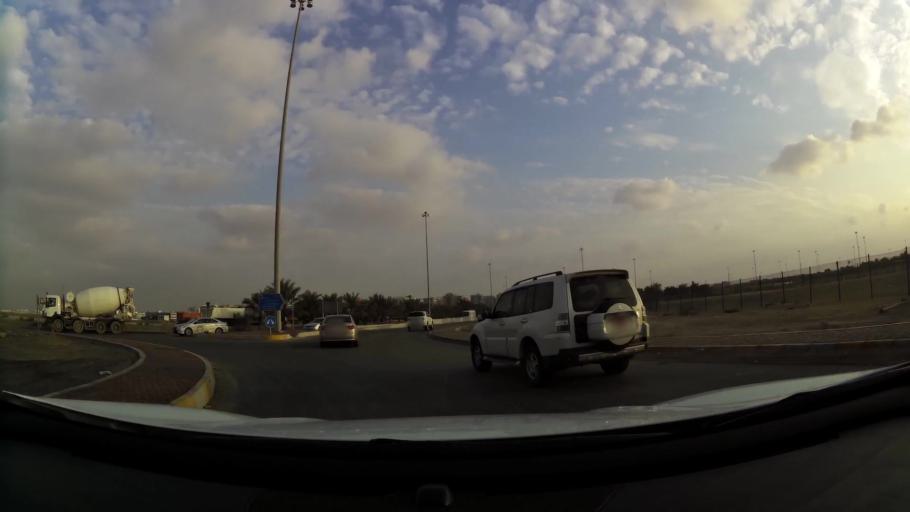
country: AE
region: Abu Dhabi
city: Abu Dhabi
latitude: 24.3512
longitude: 54.5285
